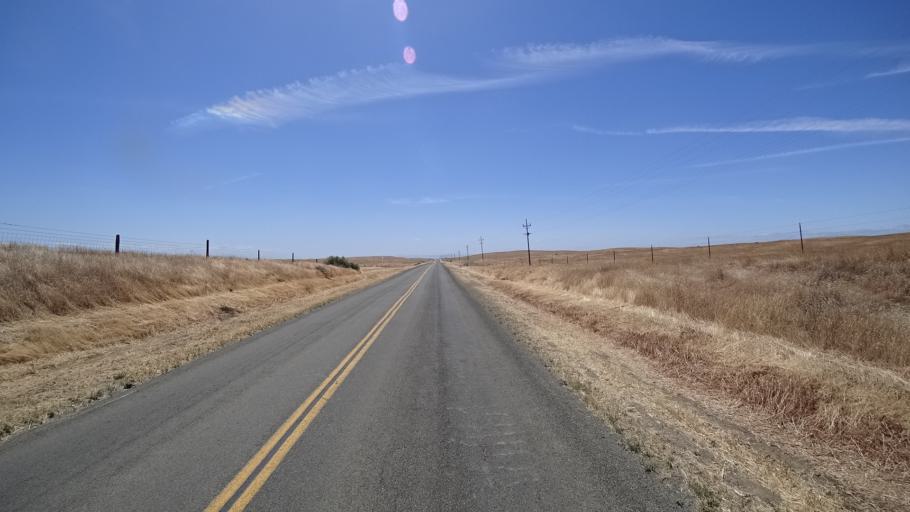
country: US
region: California
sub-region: Kings County
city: Kettleman City
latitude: 35.8844
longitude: -119.9152
